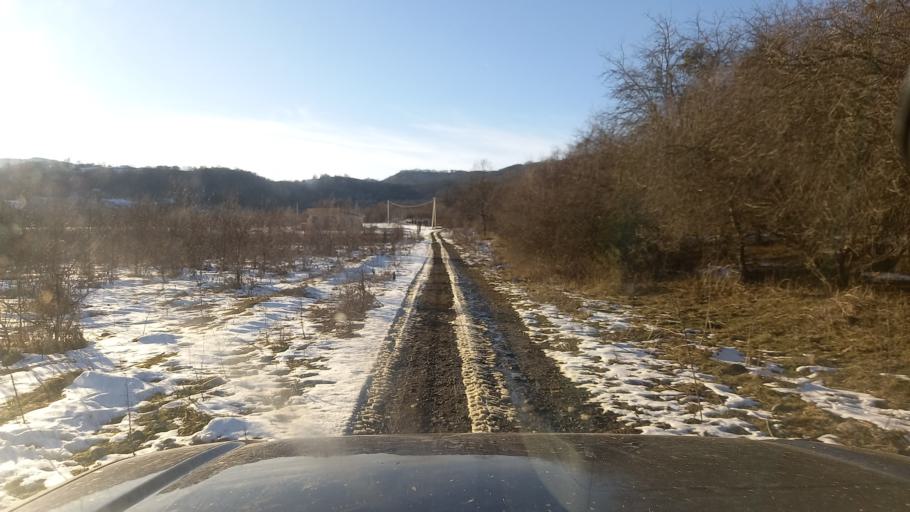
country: RU
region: Adygeya
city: Kamennomostskiy
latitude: 44.2288
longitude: 40.1706
